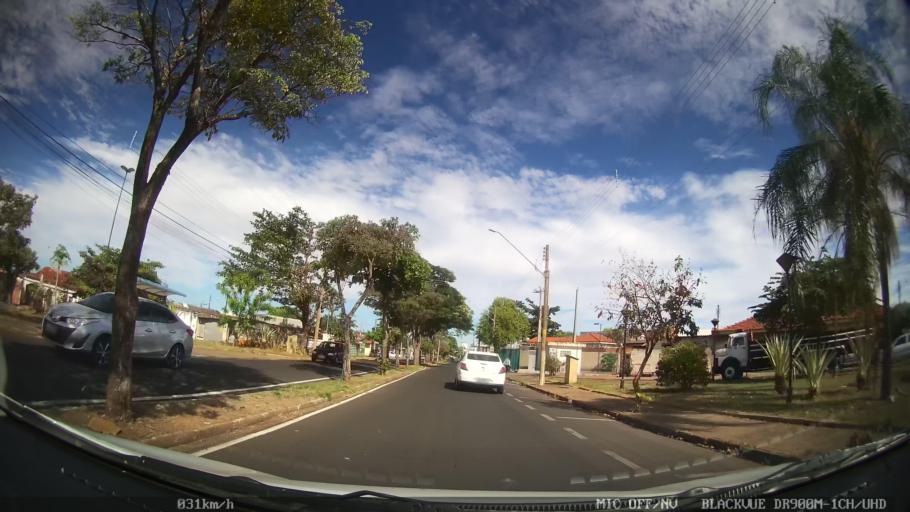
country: BR
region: Sao Paulo
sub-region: Catanduva
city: Catanduva
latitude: -21.1276
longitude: -48.9516
